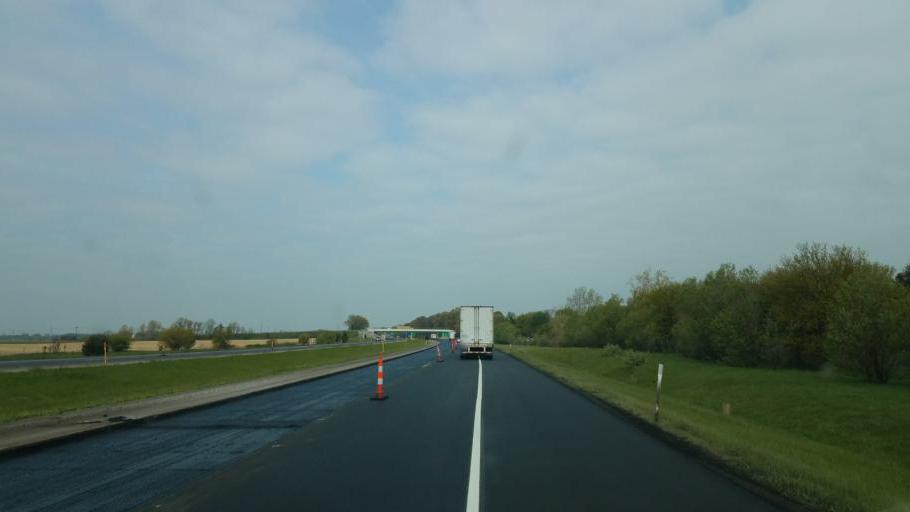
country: US
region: Indiana
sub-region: Saint Joseph County
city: Granger
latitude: 41.7333
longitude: -86.1042
